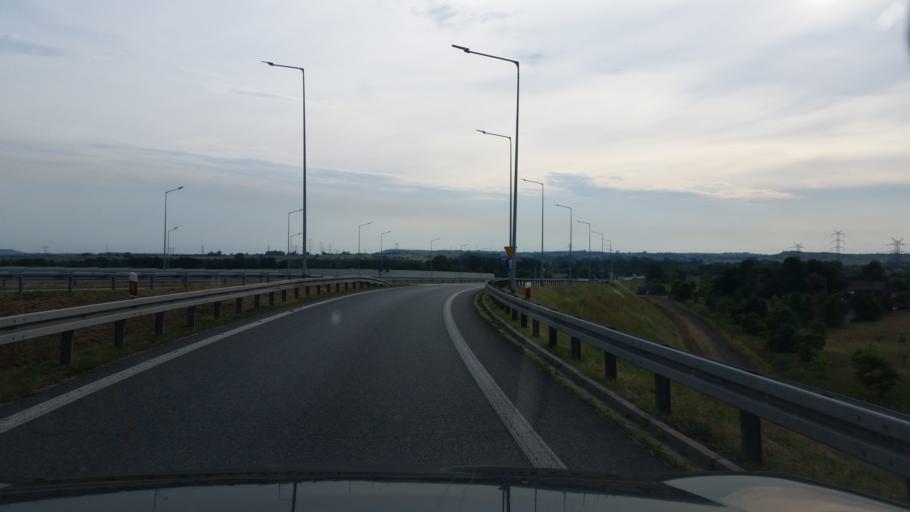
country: PL
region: Silesian Voivodeship
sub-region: Powiat bedzinski
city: Siewierz
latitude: 50.4206
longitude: 19.2080
